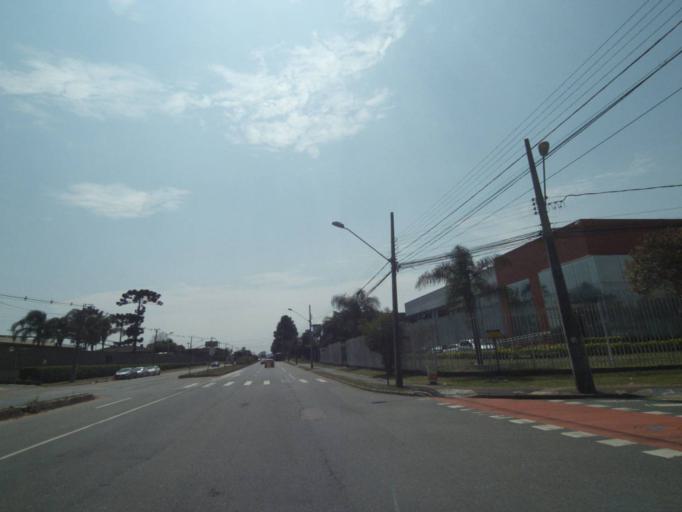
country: BR
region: Parana
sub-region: Curitiba
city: Curitiba
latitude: -25.4910
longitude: -49.3221
